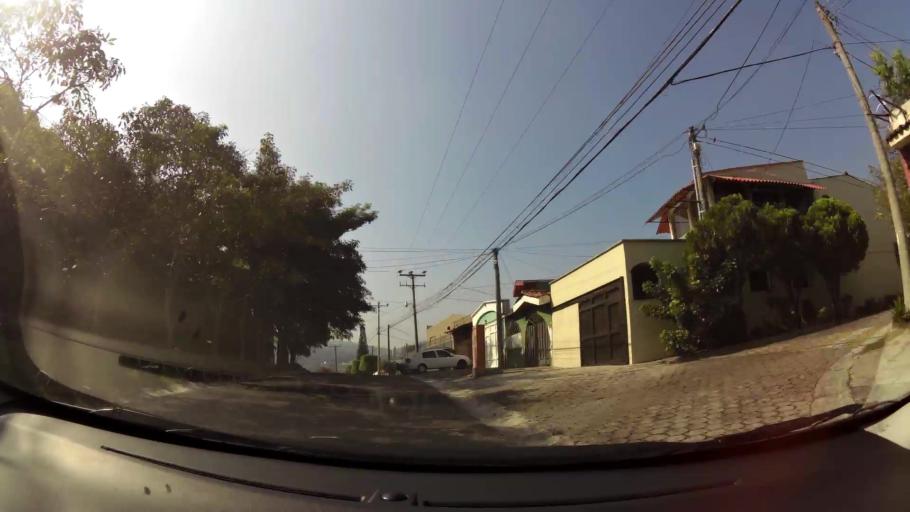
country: SV
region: La Libertad
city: Antiguo Cuscatlan
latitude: 13.6793
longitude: -89.2310
